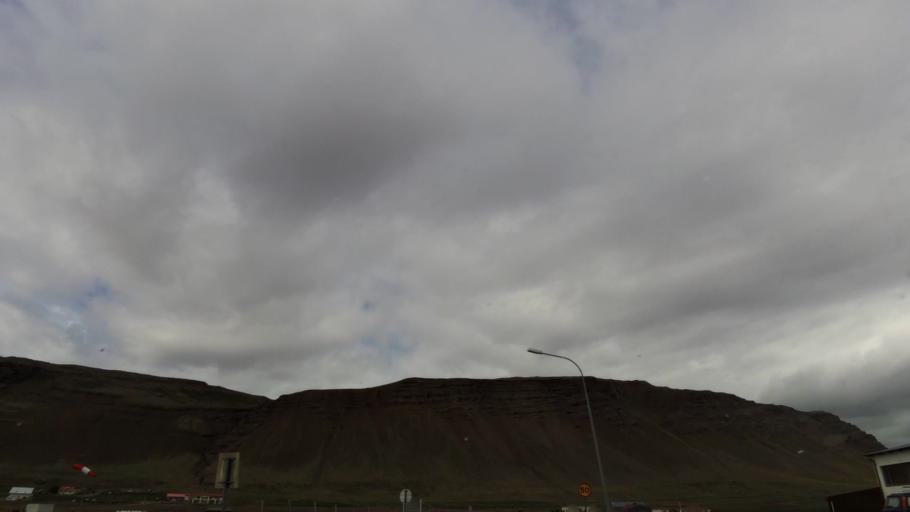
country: IS
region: West
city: Stykkisholmur
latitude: 65.4518
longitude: -22.2020
